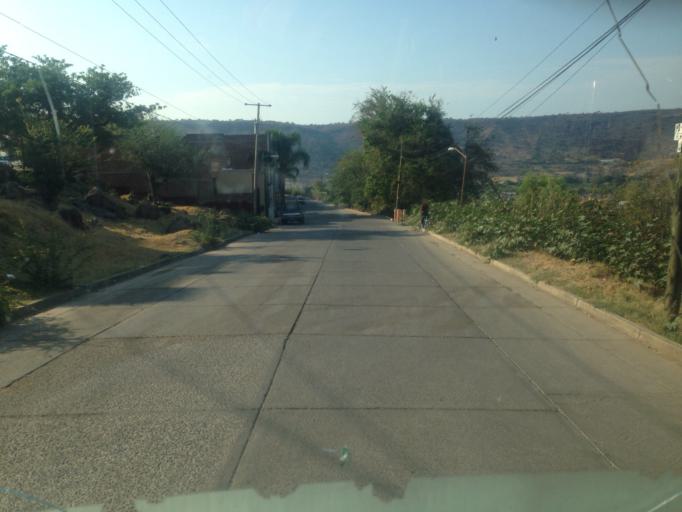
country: MX
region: Jalisco
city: Atotonilco el Alto
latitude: 20.5608
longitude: -102.5066
